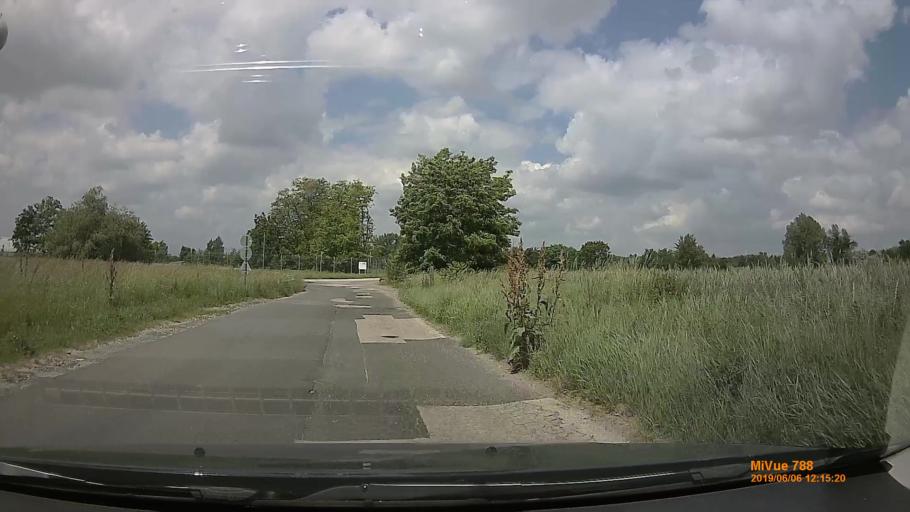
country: HU
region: Pest
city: Mogyorod
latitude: 47.5912
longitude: 19.2466
